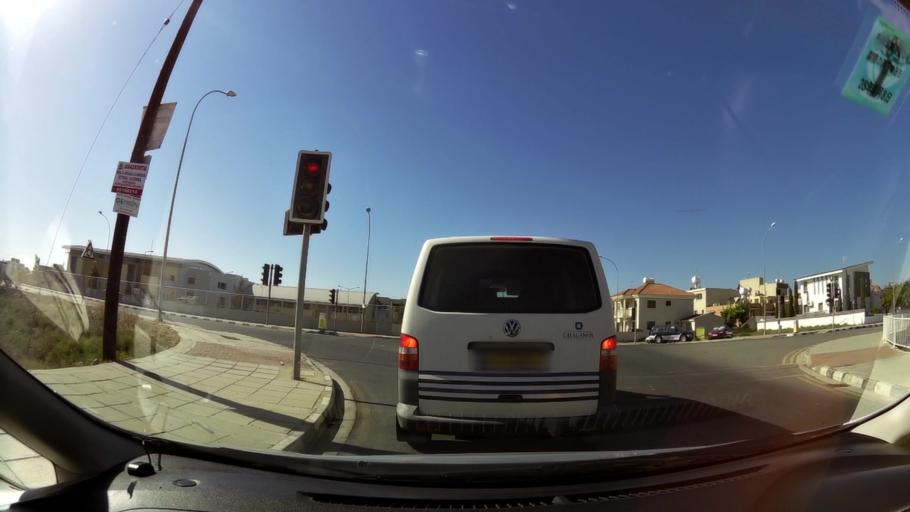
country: CY
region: Larnaka
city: Livadia
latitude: 34.9397
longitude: 33.6284
